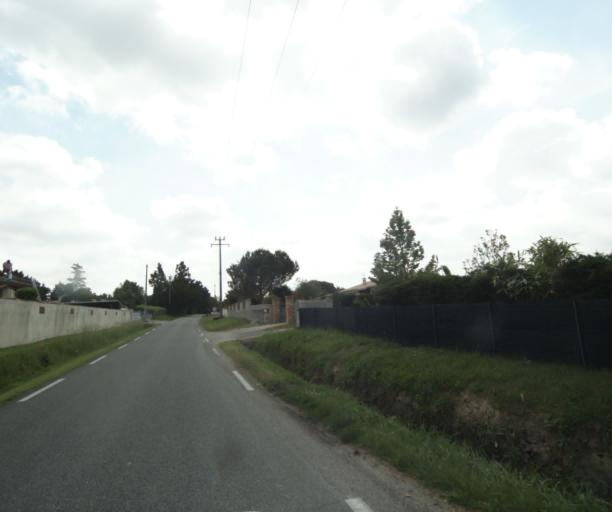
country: FR
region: Midi-Pyrenees
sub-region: Departement du Tarn-et-Garonne
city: Albias
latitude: 44.0568
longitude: 1.3989
